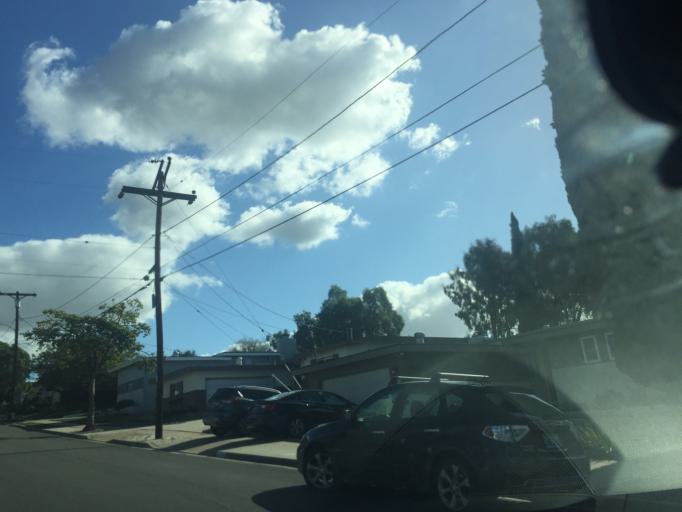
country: US
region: California
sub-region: San Diego County
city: La Mesa
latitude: 32.7841
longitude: -117.0940
